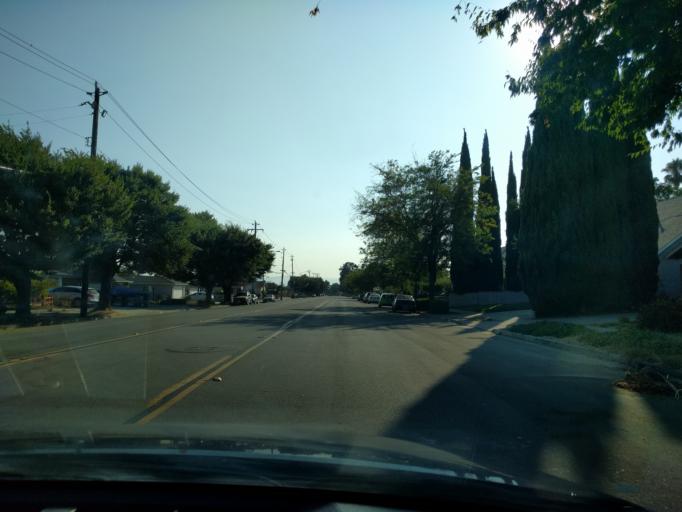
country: US
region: California
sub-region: Santa Clara County
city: East Foothills
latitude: 37.3967
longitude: -121.8539
